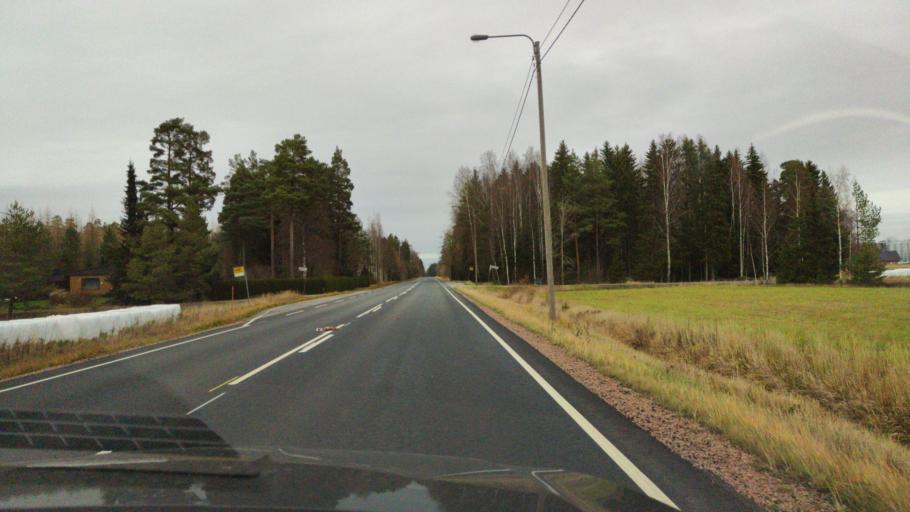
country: FI
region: Varsinais-Suomi
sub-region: Turku
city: Vahto
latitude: 60.6537
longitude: 22.4304
